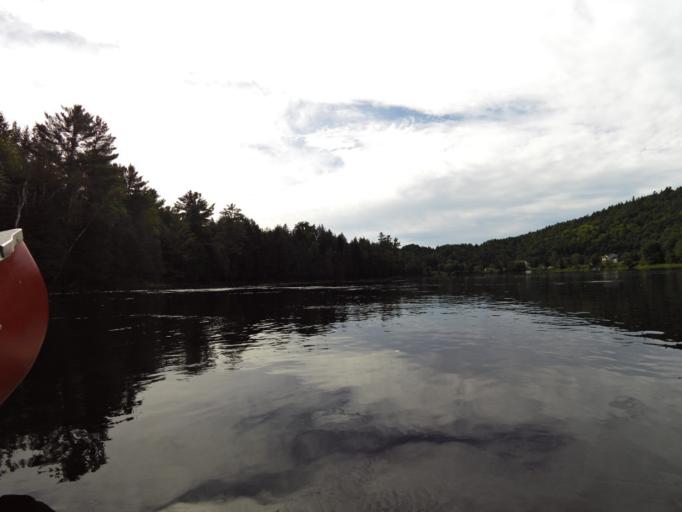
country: CA
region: Quebec
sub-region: Outaouais
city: Wakefield
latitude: 45.7766
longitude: -75.9400
